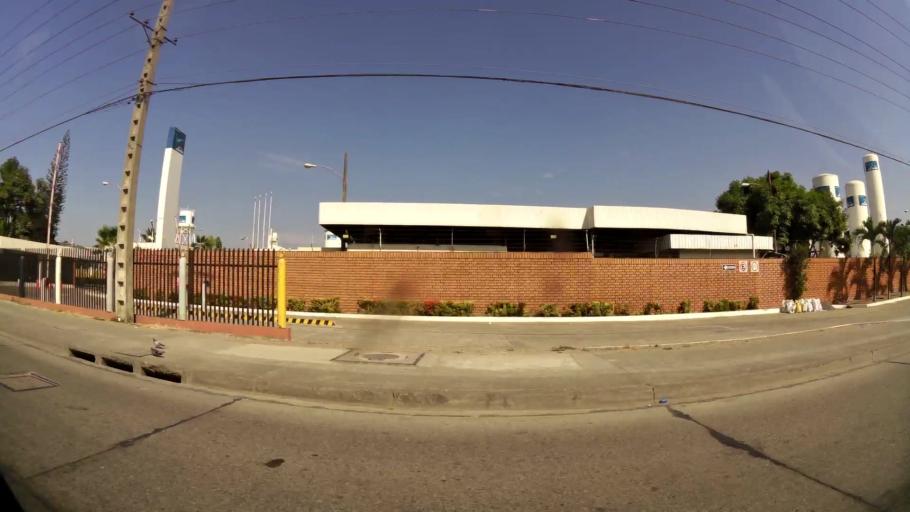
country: EC
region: Guayas
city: Santa Lucia
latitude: -2.1024
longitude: -79.9355
